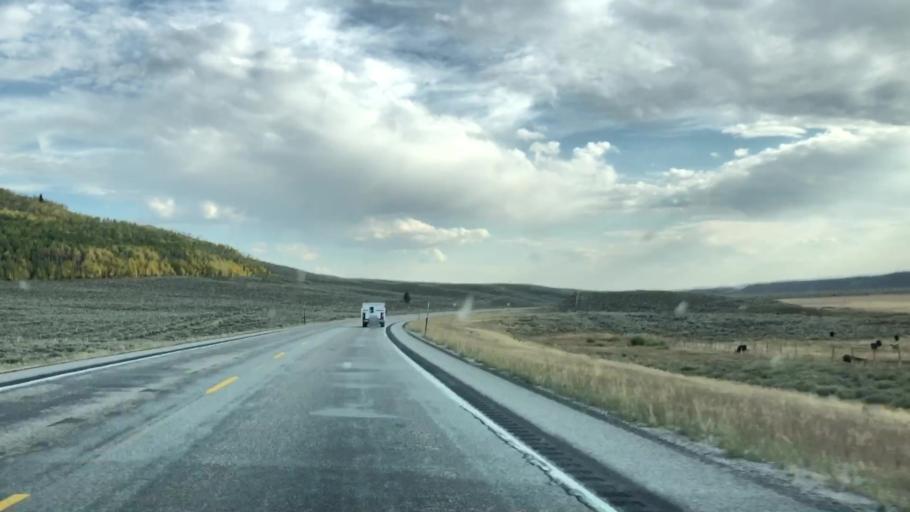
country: US
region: Wyoming
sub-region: Sublette County
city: Pinedale
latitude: 43.0865
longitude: -110.1631
